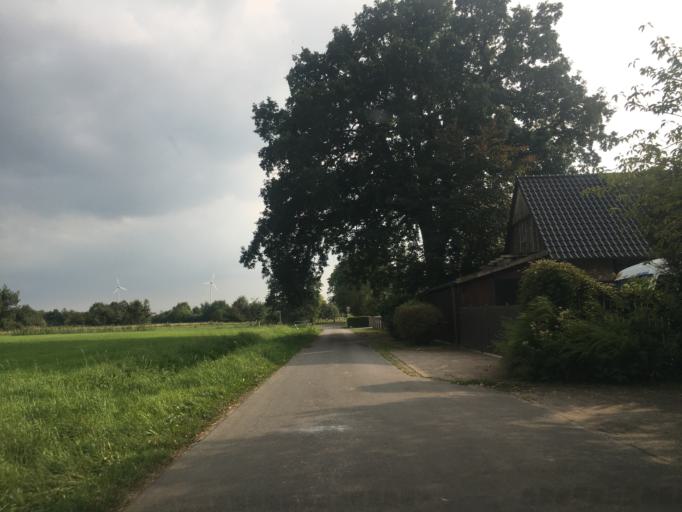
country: DE
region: North Rhine-Westphalia
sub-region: Regierungsbezirk Munster
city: Greven
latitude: 52.0424
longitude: 7.5823
